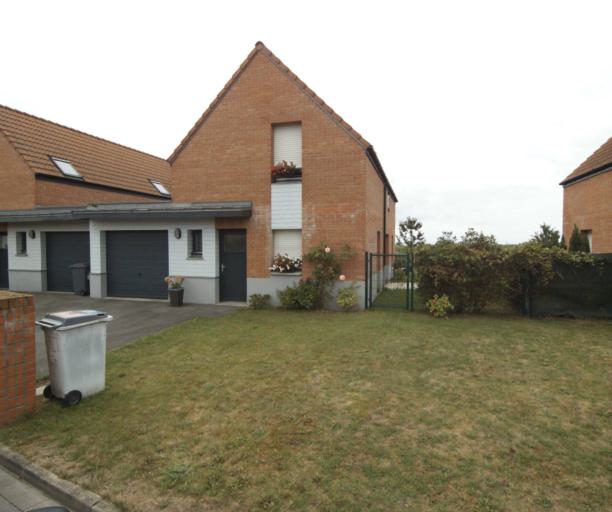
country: FR
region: Nord-Pas-de-Calais
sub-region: Departement du Nord
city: Faches-Thumesnil
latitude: 50.5907
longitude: 3.0710
